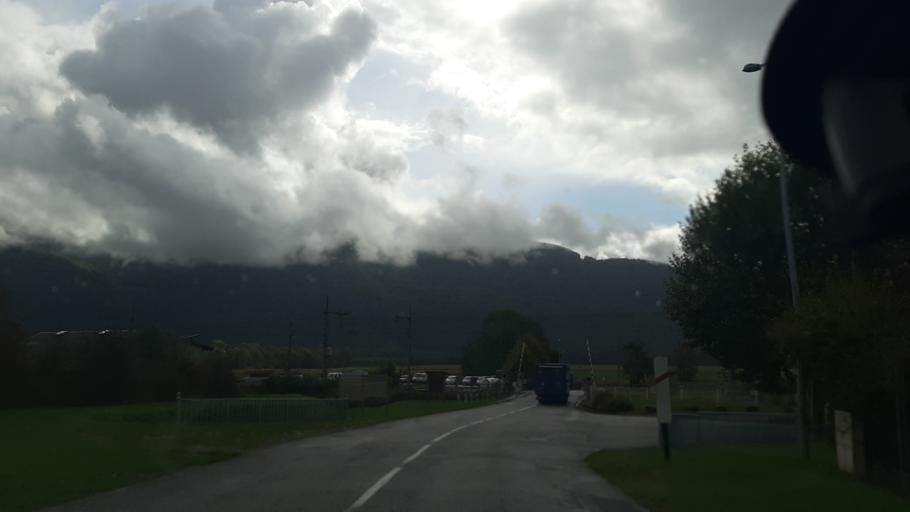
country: FR
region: Rhone-Alpes
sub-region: Departement de la Savoie
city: Gresy-sur-Isere
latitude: 45.5951
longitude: 6.2601
